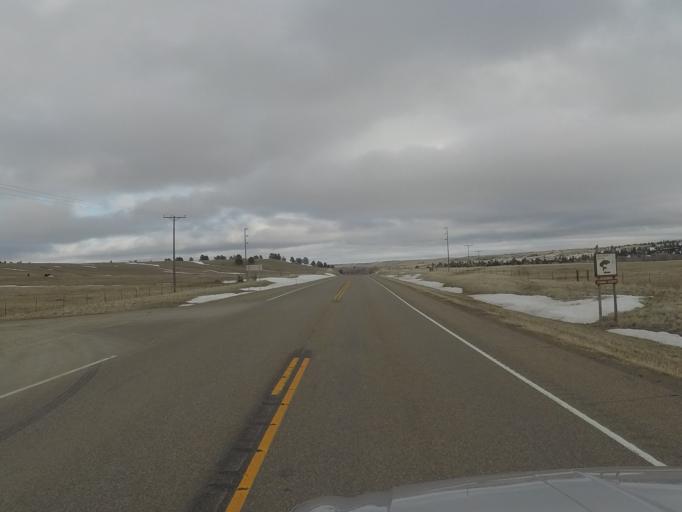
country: US
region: Montana
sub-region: Golden Valley County
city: Ryegate
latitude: 46.3229
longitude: -109.4466
